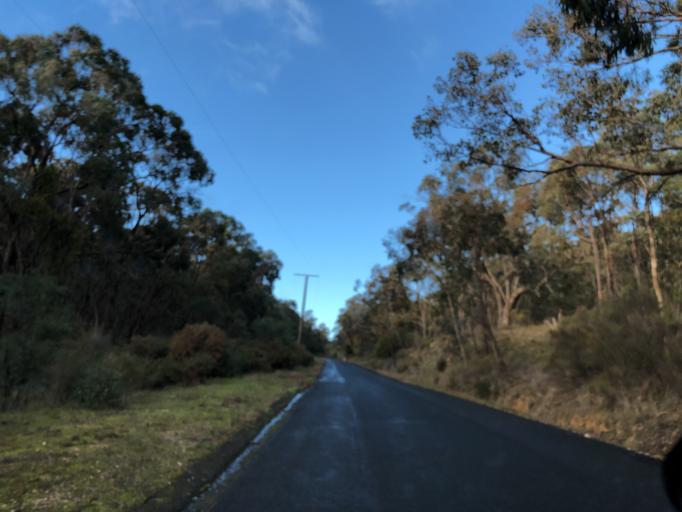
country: AU
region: Victoria
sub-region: Mount Alexander
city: Castlemaine
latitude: -37.2083
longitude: 144.2859
